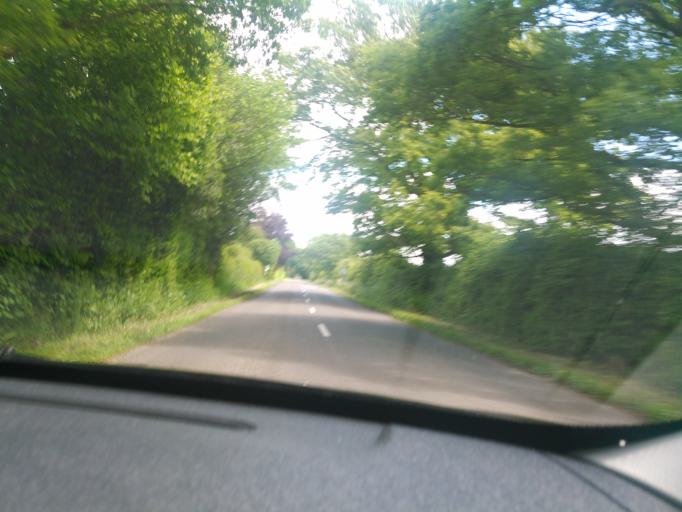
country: GB
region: England
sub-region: Shropshire
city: Prees
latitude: 52.8830
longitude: -2.6458
